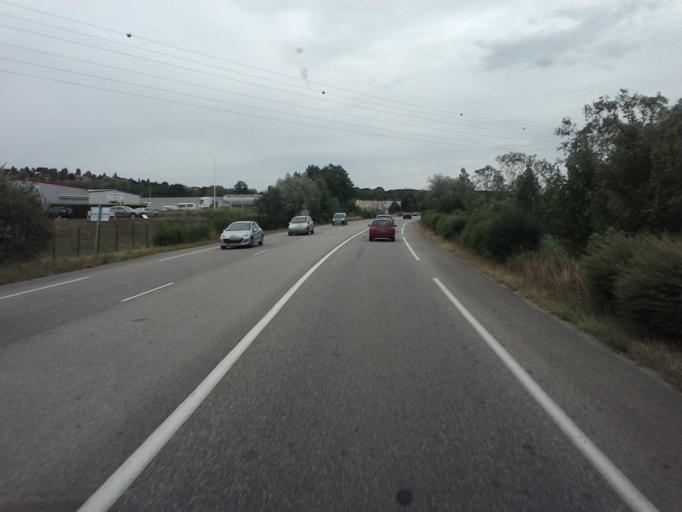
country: FR
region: Lorraine
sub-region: Departement de Meurthe-et-Moselle
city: Richardmenil
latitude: 48.6080
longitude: 6.1668
